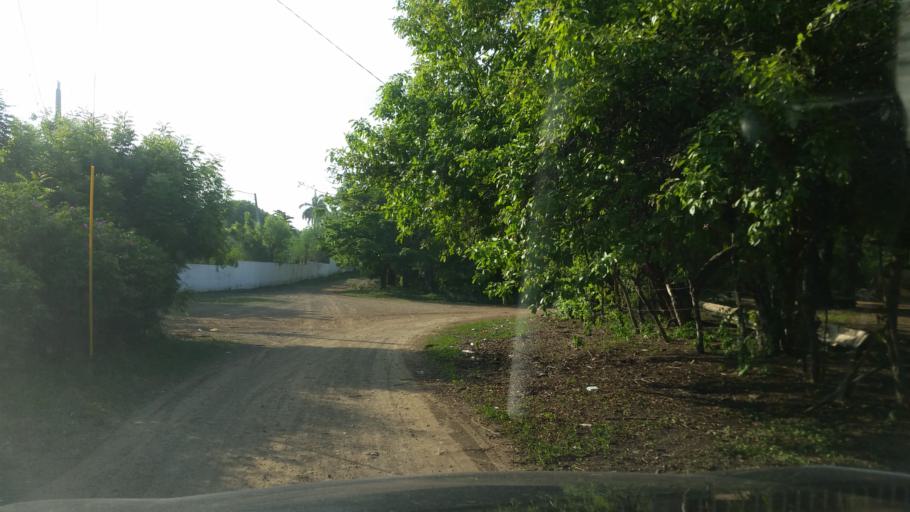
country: NI
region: Managua
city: Masachapa
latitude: 11.7584
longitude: -86.4907
